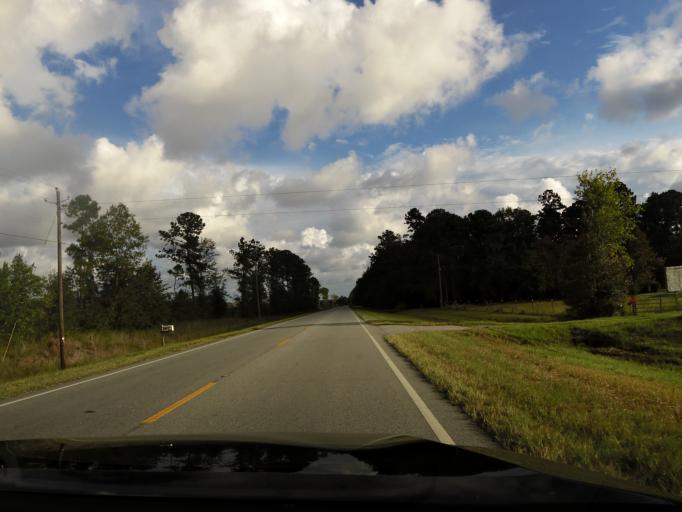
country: US
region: Georgia
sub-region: Liberty County
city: Midway
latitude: 31.7602
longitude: -81.4454
